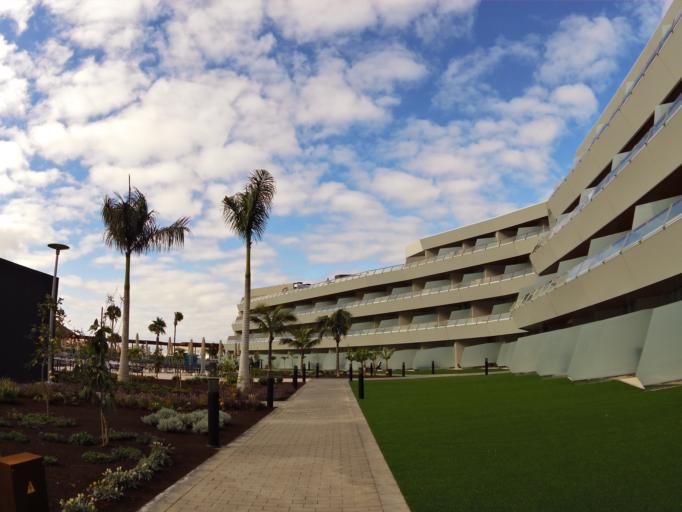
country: ES
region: Canary Islands
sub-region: Provincia de Las Palmas
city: Puerto Rico
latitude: 27.8269
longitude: -15.7577
